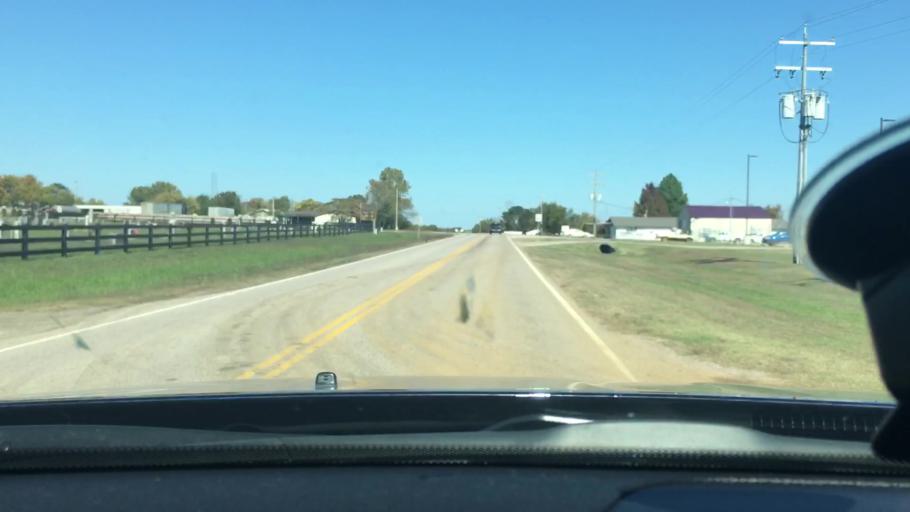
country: US
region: Oklahoma
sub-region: Johnston County
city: Tishomingo
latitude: 34.4412
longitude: -96.6359
